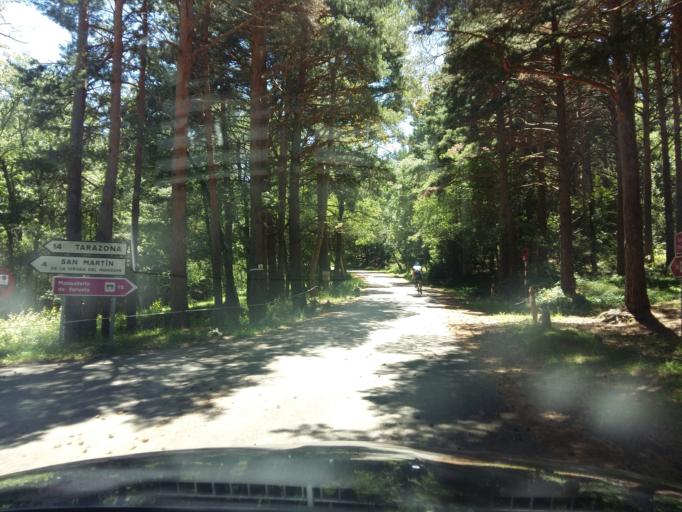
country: ES
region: Castille and Leon
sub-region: Provincia de Soria
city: Vozmediano
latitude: 41.8163
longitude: -1.8222
